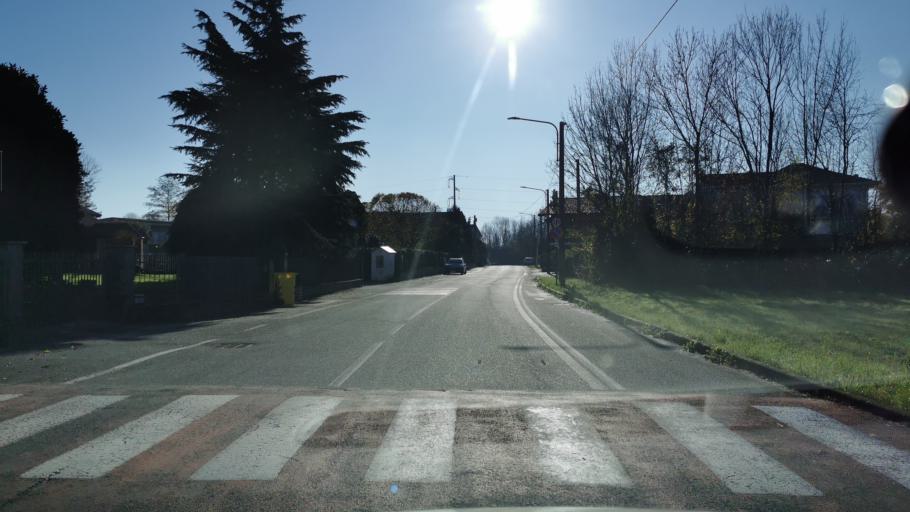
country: IT
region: Piedmont
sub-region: Provincia di Torino
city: Fiano
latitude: 45.2103
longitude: 7.5260
